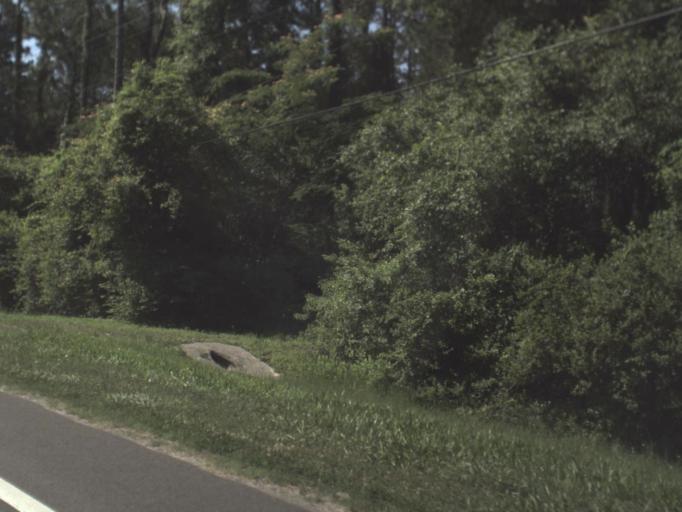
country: US
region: Florida
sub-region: Nassau County
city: Callahan
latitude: 30.5550
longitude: -81.8090
